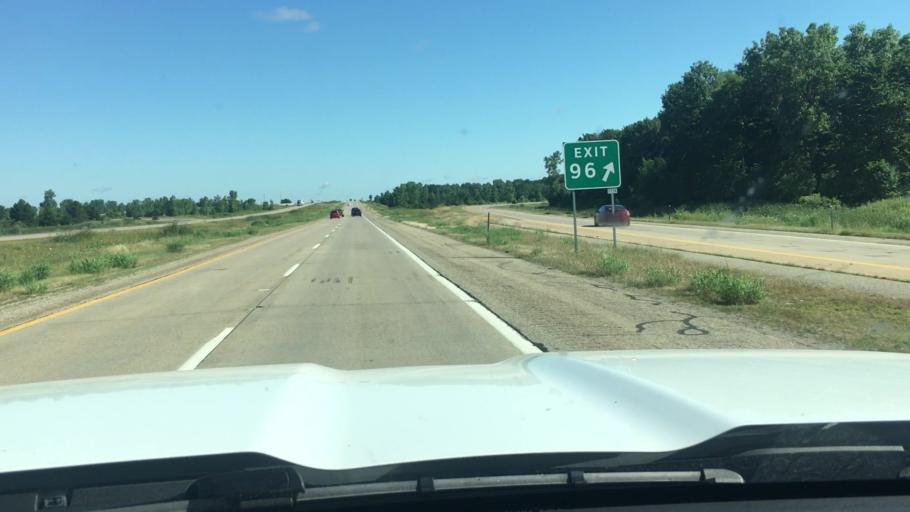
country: US
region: Michigan
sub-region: Clinton County
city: Saint Johns
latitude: 42.9940
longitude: -84.5186
